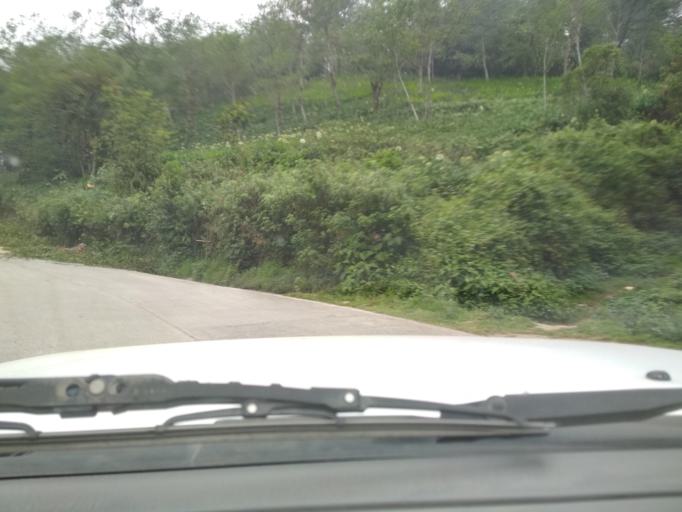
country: MX
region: Veracruz
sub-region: La Perla
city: Metlac Hernandez (Metlac Primero)
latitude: 18.9726
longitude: -97.1524
